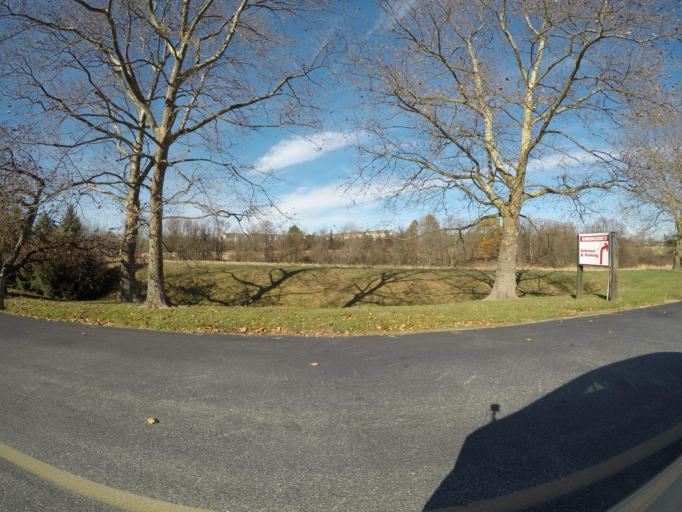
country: US
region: Pennsylvania
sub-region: Chester County
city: Caln
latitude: 40.0108
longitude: -75.7856
